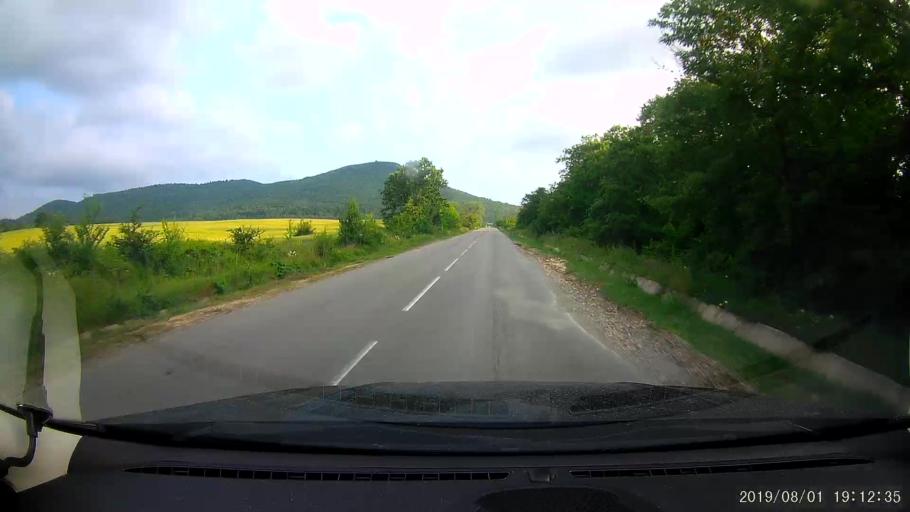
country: BG
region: Shumen
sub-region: Obshtina Smyadovo
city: Smyadovo
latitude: 42.9628
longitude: 26.9495
